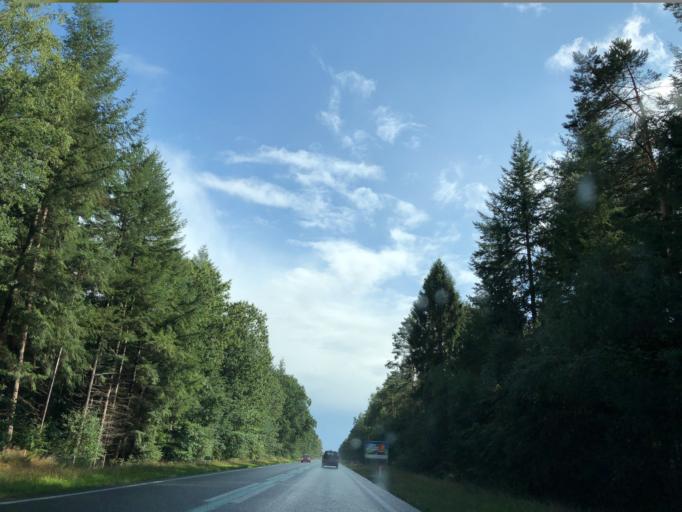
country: NL
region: Drenthe
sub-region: Gemeente Borger-Odoorn
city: Borger
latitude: 52.9596
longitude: 6.7809
